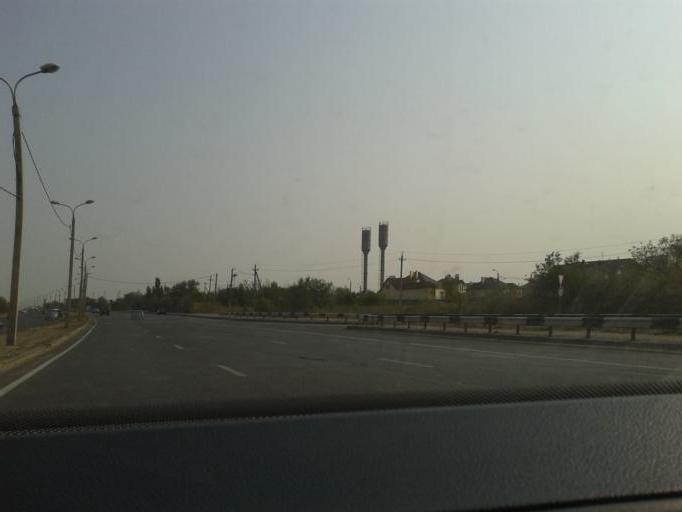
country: RU
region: Volgograd
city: Volgograd
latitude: 48.7331
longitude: 44.4547
